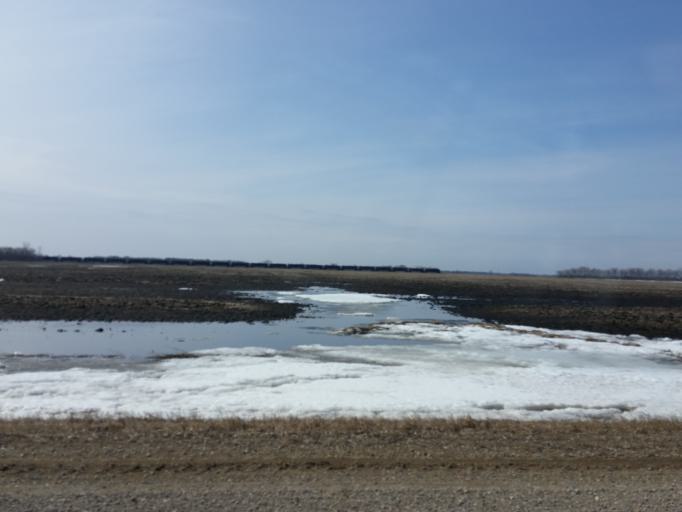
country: US
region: North Dakota
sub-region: Walsh County
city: Grafton
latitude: 48.4352
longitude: -97.4055
